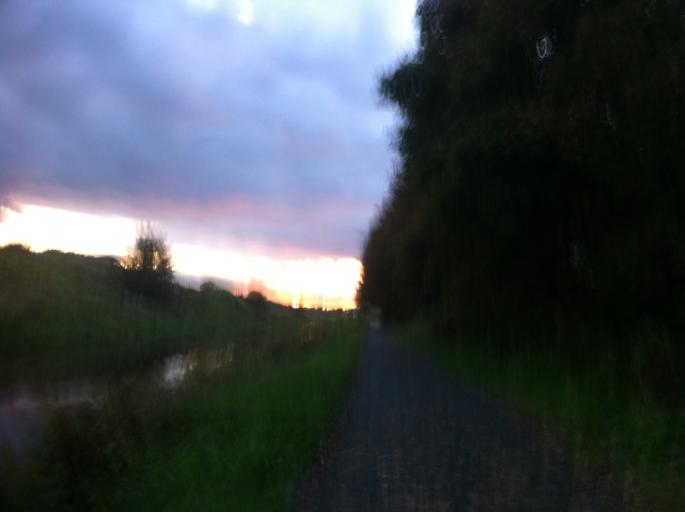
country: GB
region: Scotland
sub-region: East Dunbartonshire
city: Kirkintilloch
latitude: 55.9310
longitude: -4.1775
